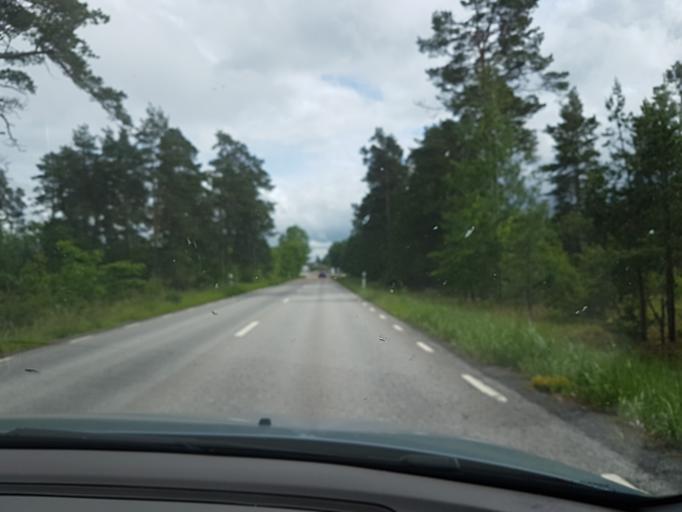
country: SE
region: Uppsala
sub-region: Osthammars Kommun
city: OEsthammar
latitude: 60.2575
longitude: 18.3428
